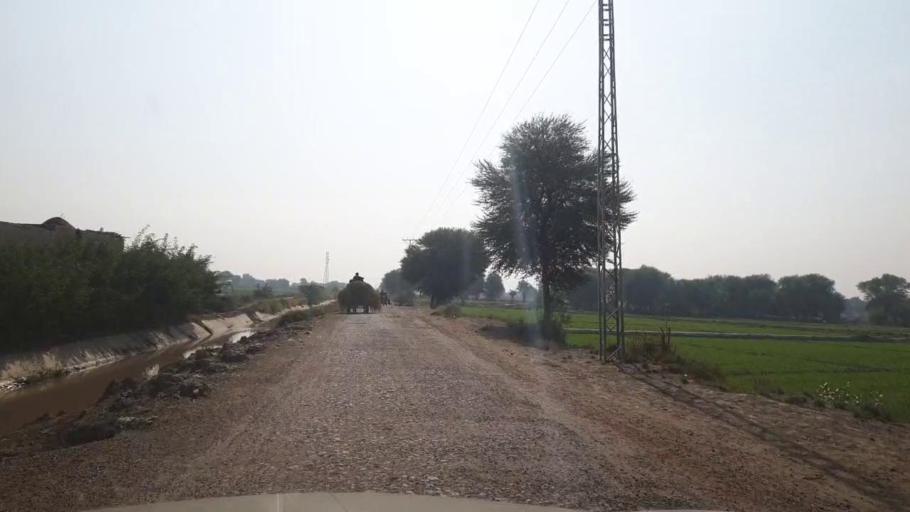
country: PK
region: Sindh
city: Bhan
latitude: 26.5347
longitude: 67.7764
